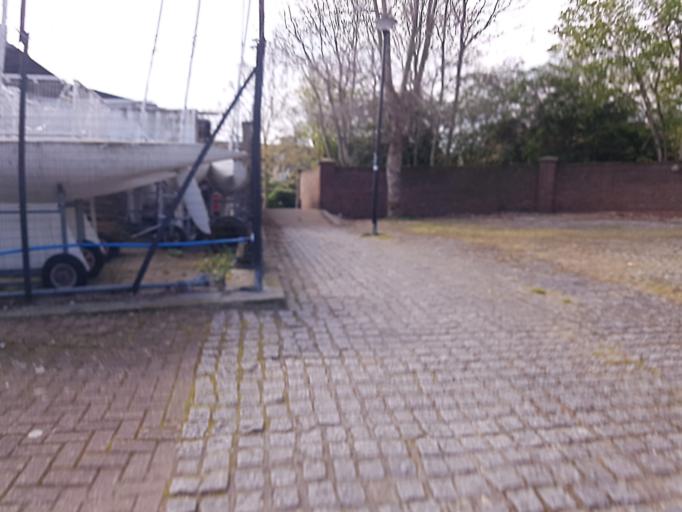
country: GB
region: England
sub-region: Greater London
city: Poplar
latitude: 51.4946
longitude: -0.0241
